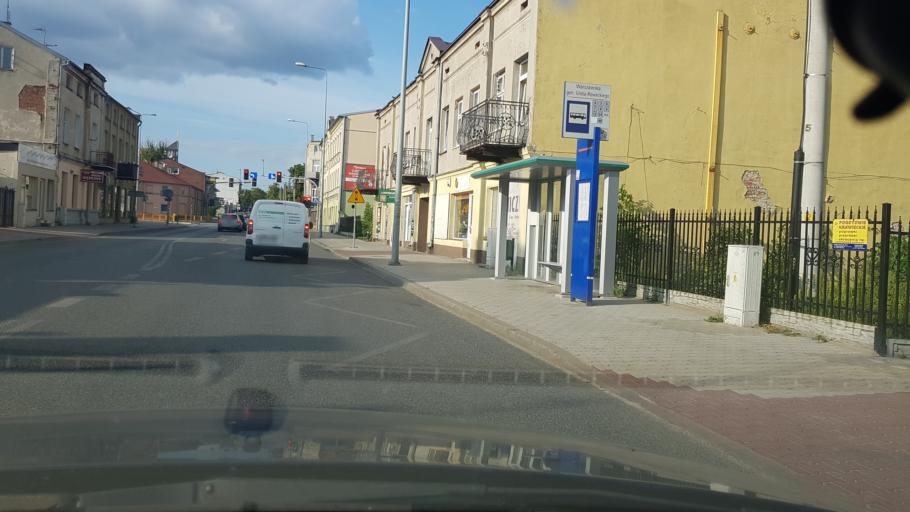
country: PL
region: Lodz Voivodeship
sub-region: Powiat tomaszowski
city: Tomaszow Mazowiecki
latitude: 51.5388
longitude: 20.0110
